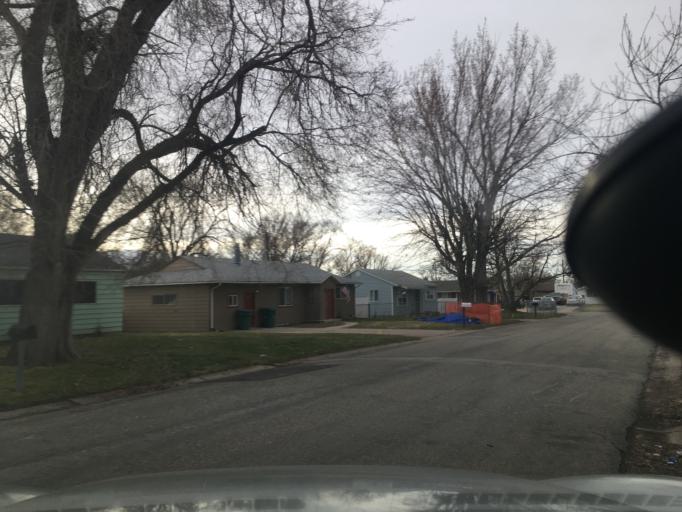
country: US
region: Utah
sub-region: Davis County
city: Layton
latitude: 41.0722
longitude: -111.9707
